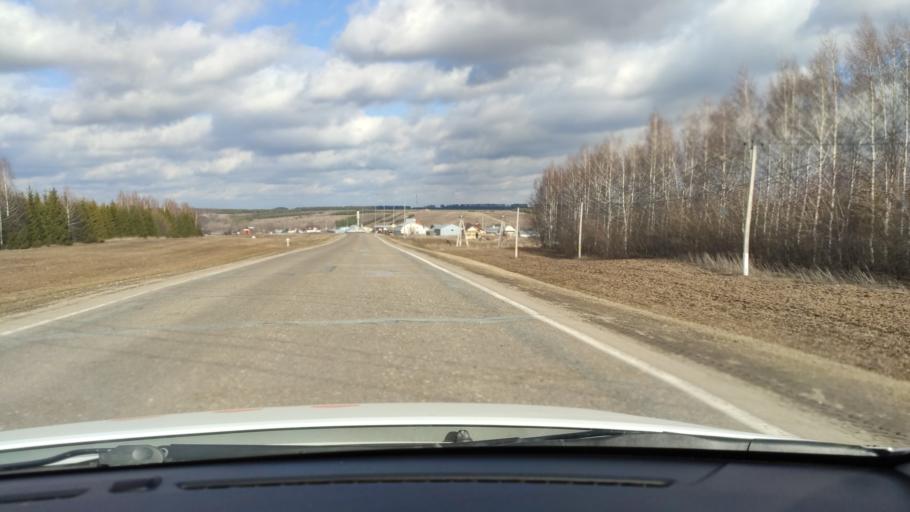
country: RU
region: Tatarstan
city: Vysokaya Gora
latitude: 56.1166
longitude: 49.1918
